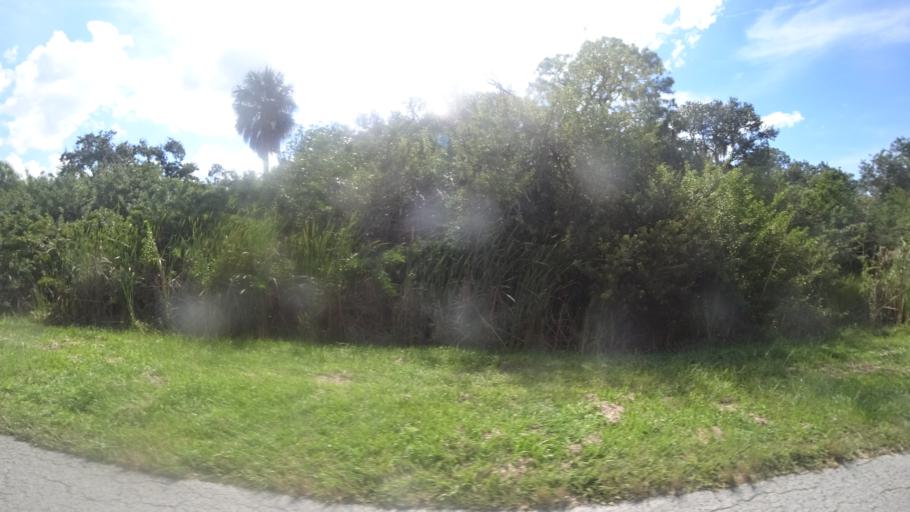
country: US
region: Florida
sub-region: Manatee County
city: Memphis
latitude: 27.6399
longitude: -82.5516
